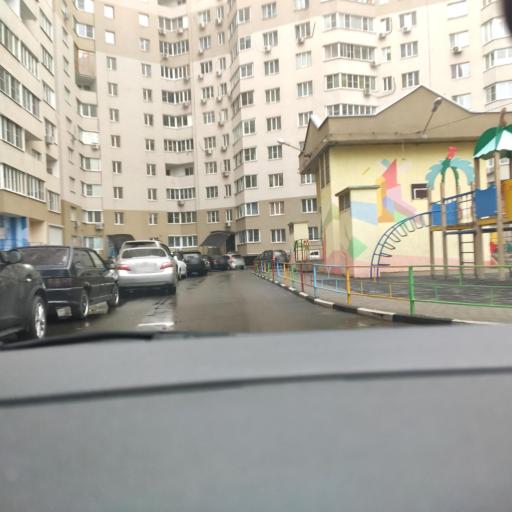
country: RU
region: Voronezj
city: Voronezh
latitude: 51.6744
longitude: 39.1947
